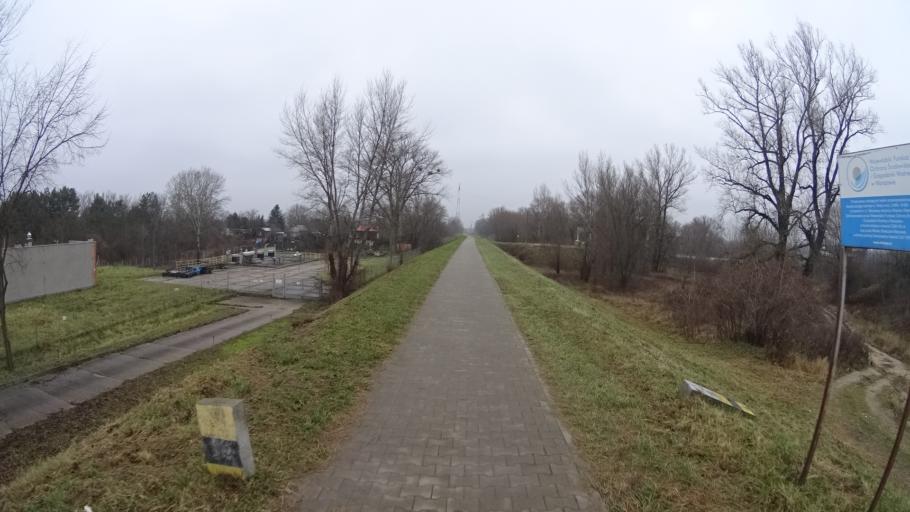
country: PL
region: Masovian Voivodeship
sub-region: Warszawa
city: Wilanow
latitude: 52.1911
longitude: 21.1024
